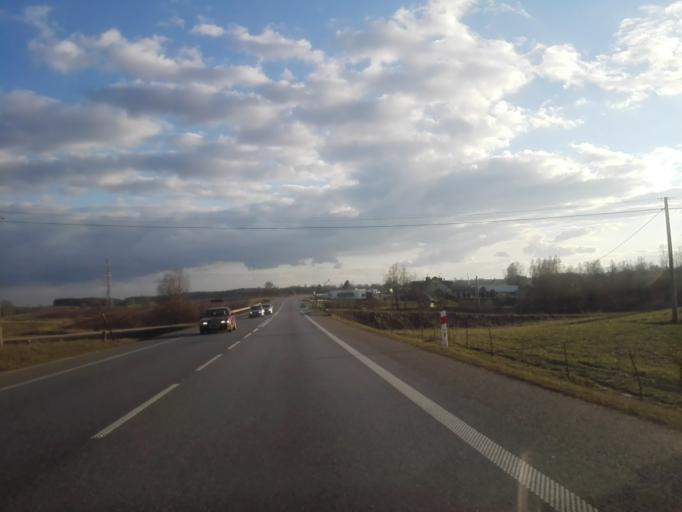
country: PL
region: Podlasie
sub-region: Suwalki
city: Suwalki
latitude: 54.1803
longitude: 22.9993
